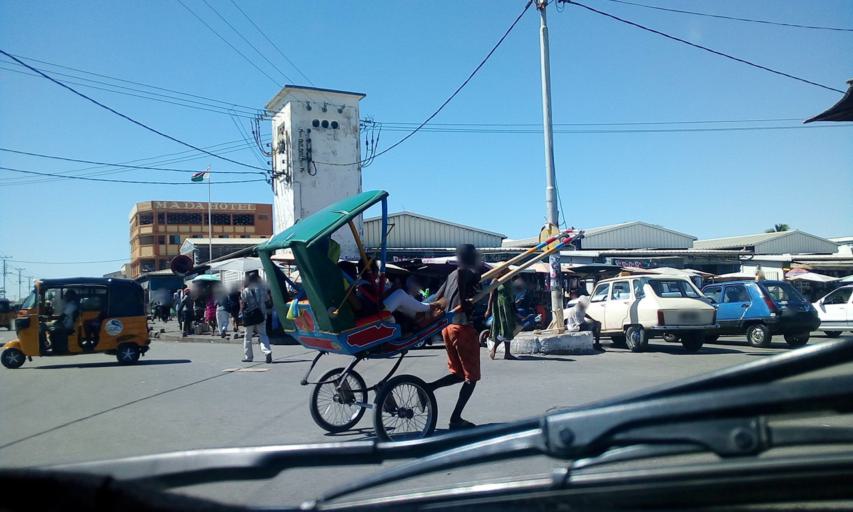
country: MG
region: Boeny
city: Mahajanga
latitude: -15.7178
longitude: 46.3197
